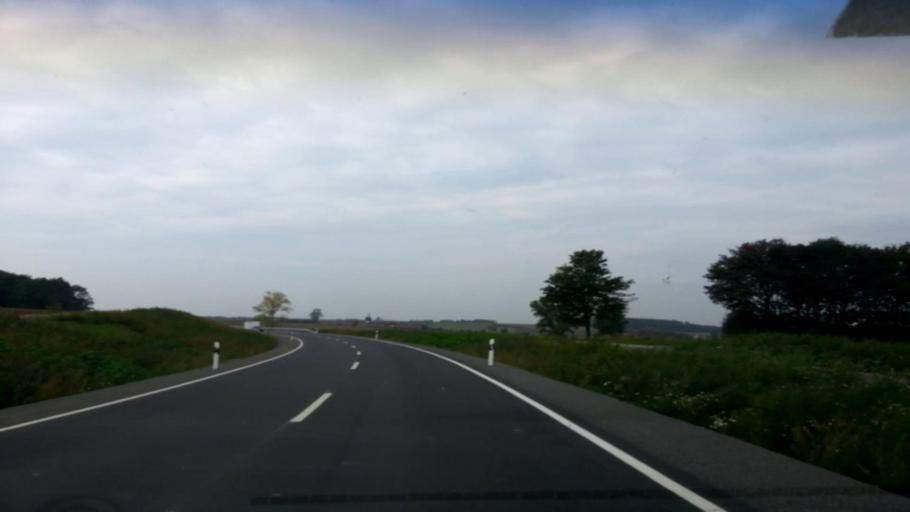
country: DE
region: Bavaria
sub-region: Regierungsbezirk Unterfranken
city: Donnersdorf
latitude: 49.9563
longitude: 10.4032
